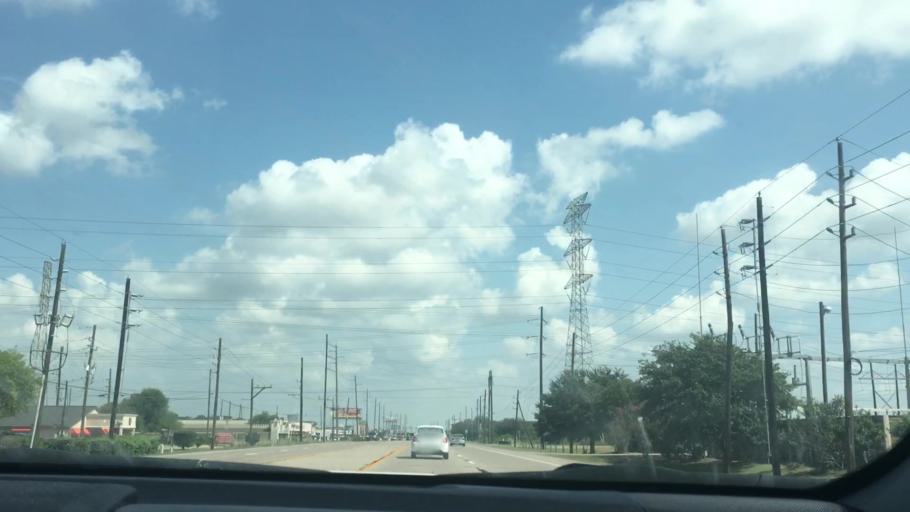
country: US
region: Texas
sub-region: Fort Bend County
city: Stafford
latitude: 29.6039
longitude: -95.5644
